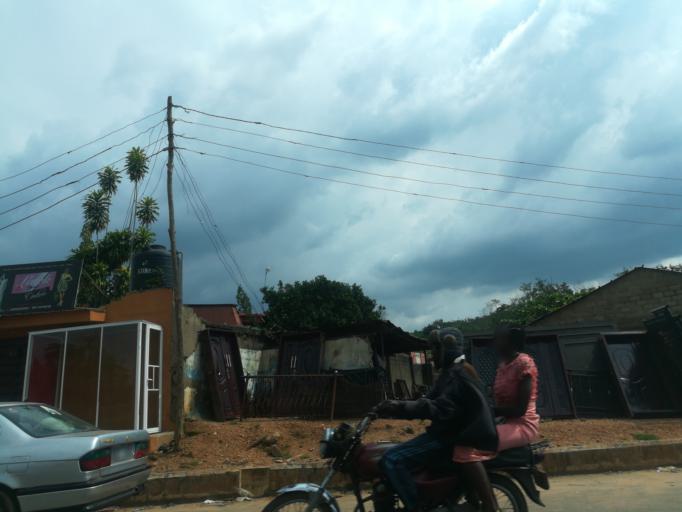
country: NG
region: Oyo
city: Ibadan
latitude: 7.4162
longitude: 3.8534
